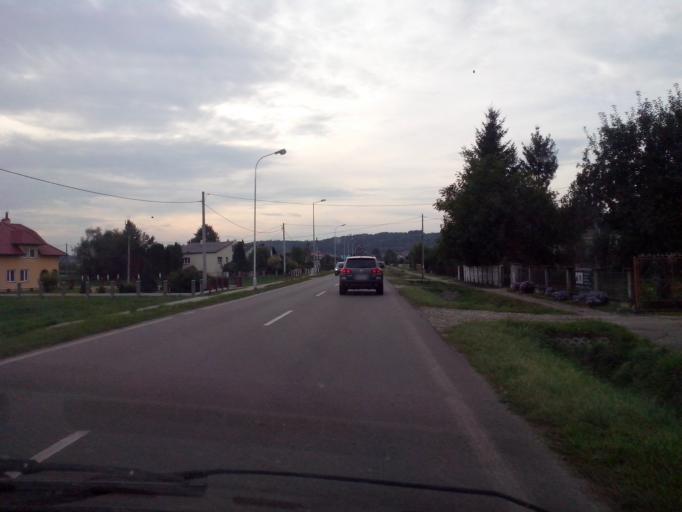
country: PL
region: Subcarpathian Voivodeship
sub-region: Powiat przemyski
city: Przedmiescie Dubieckie
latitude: 49.8280
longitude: 22.3788
